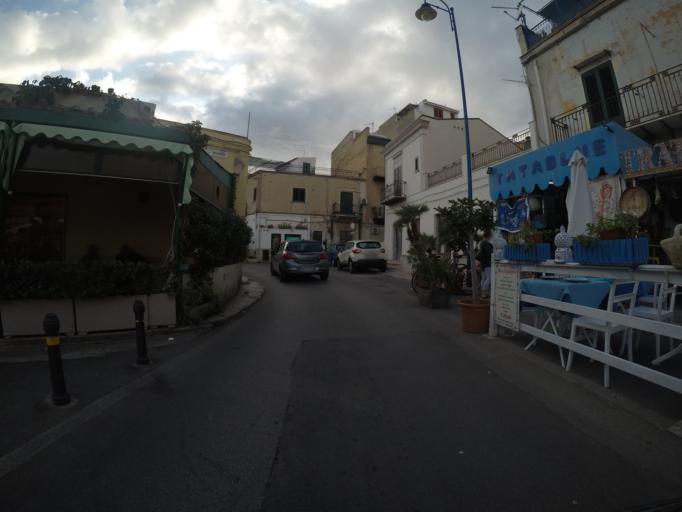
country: IT
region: Sicily
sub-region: Palermo
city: Palermo
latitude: 38.2076
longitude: 13.3261
